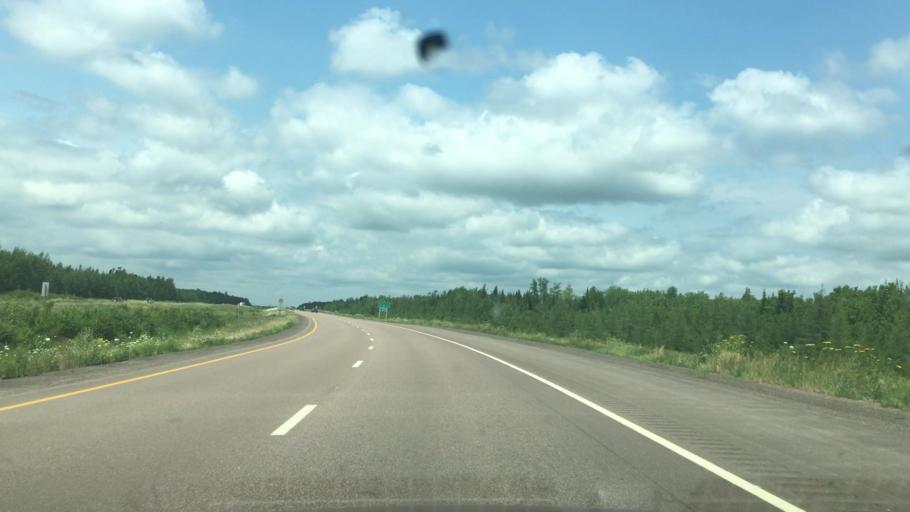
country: CA
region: New Brunswick
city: Dieppe
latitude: 46.1088
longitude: -64.6102
